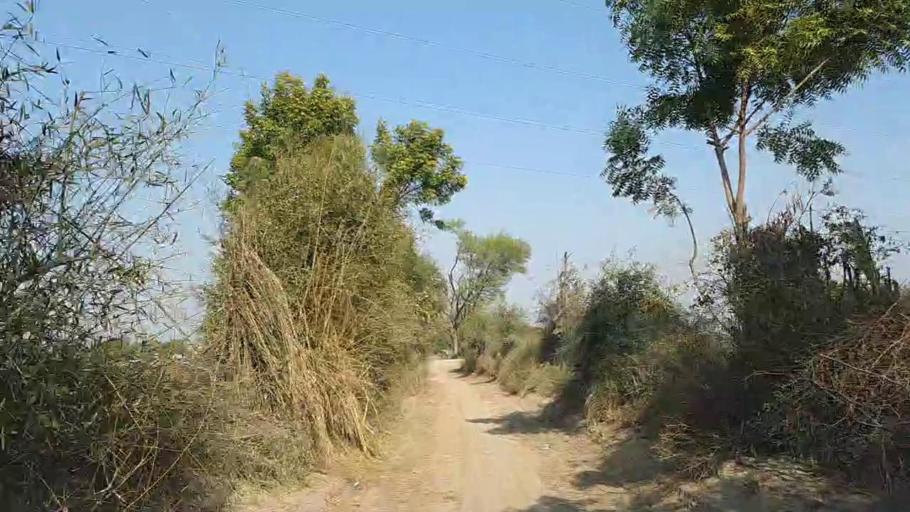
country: PK
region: Sindh
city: Moro
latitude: 26.6831
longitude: 67.9446
